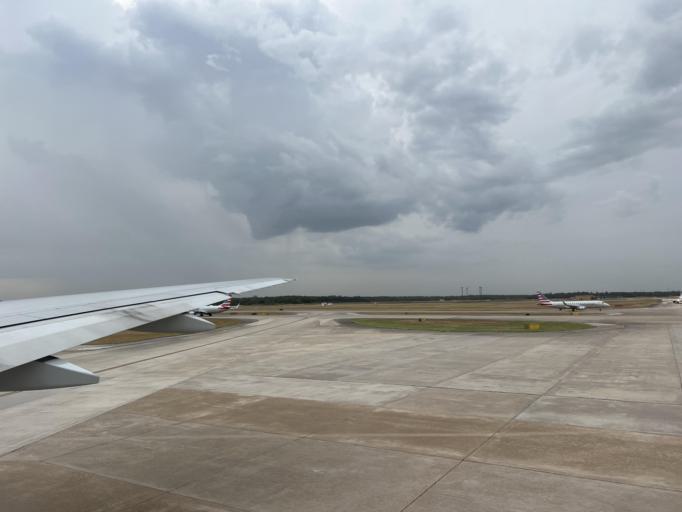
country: US
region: Texas
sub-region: Harris County
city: Aldine
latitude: 29.9892
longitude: -95.3549
